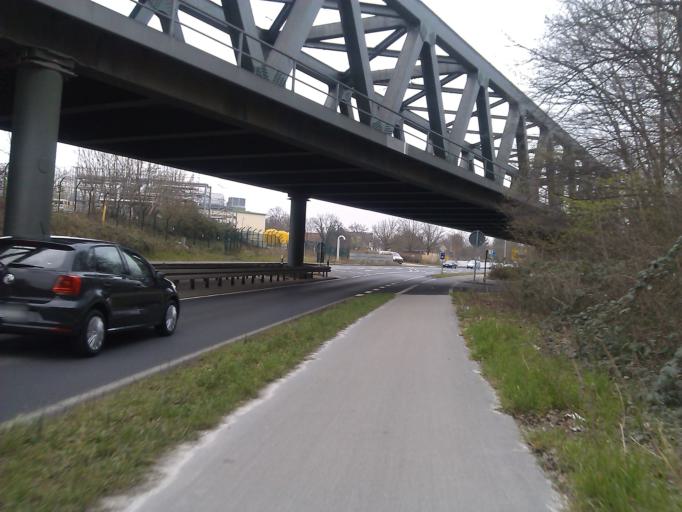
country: DE
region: North Rhine-Westphalia
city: Wesseling
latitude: 50.8437
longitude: 6.9764
